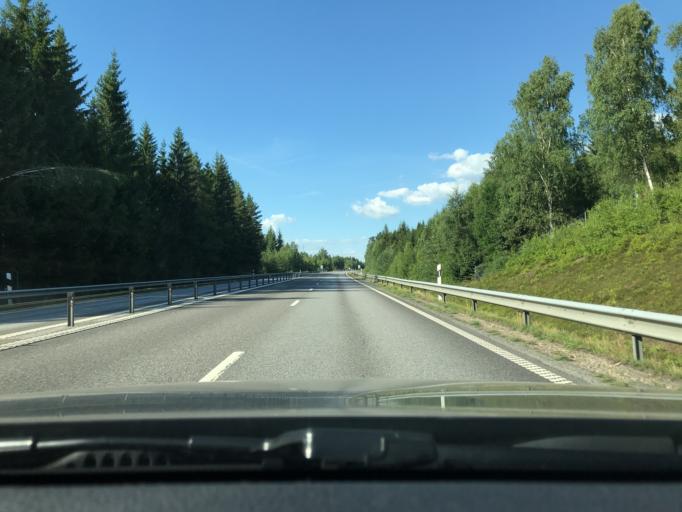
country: SE
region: Skane
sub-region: Osby Kommun
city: Osby
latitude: 56.4280
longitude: 14.0579
